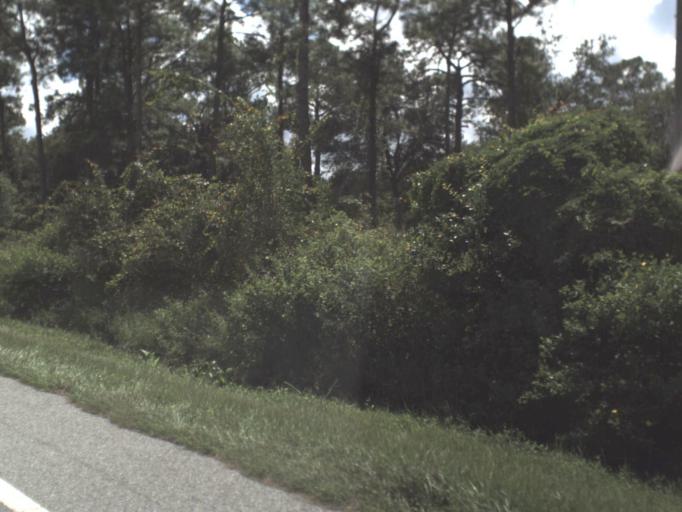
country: US
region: Florida
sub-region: DeSoto County
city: Arcadia
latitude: 27.3190
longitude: -82.1164
